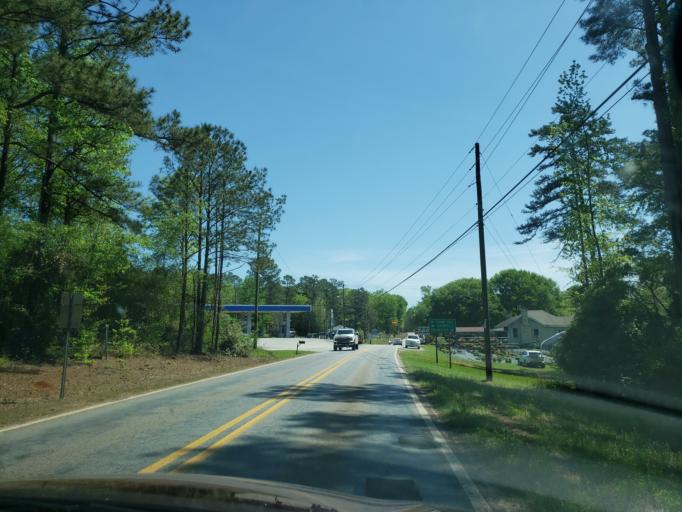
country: US
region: Alabama
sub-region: Tallapoosa County
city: Dadeville
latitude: 32.7100
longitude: -85.7870
